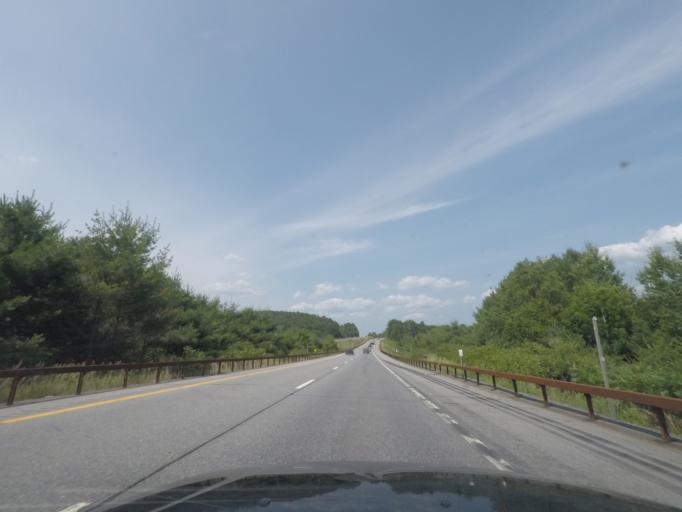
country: US
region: New York
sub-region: Warren County
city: Warrensburg
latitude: 43.7786
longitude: -73.7991
